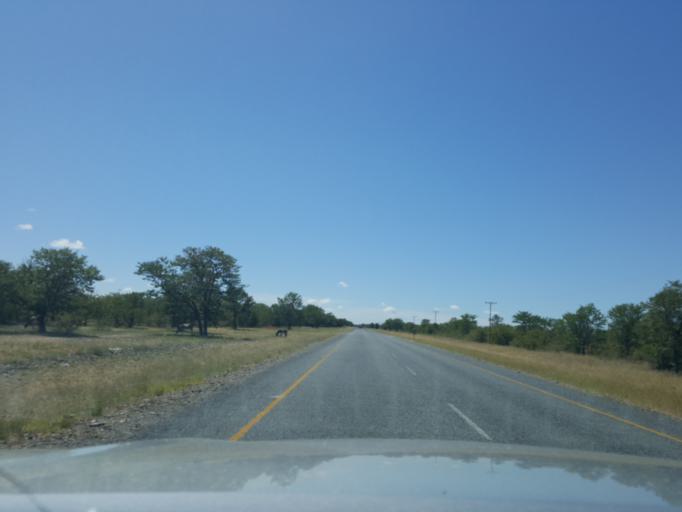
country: BW
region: Central
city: Gweta
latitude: -20.1900
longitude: 25.2544
